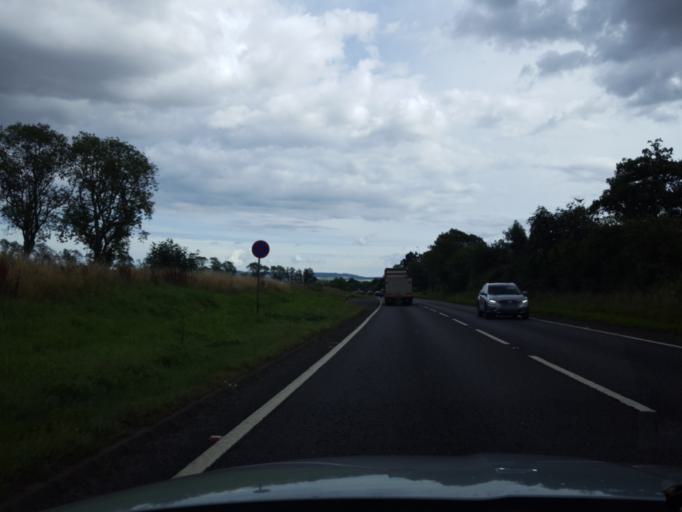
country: GB
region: Scotland
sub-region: Perth and Kinross
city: Bankfoot
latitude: 56.4829
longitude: -3.4971
